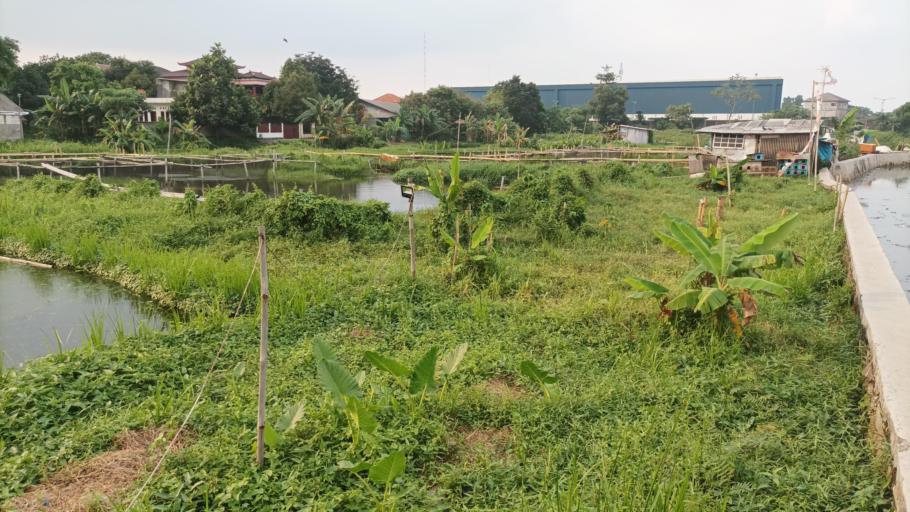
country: ID
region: West Java
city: Depok
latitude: -6.3894
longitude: 106.8700
